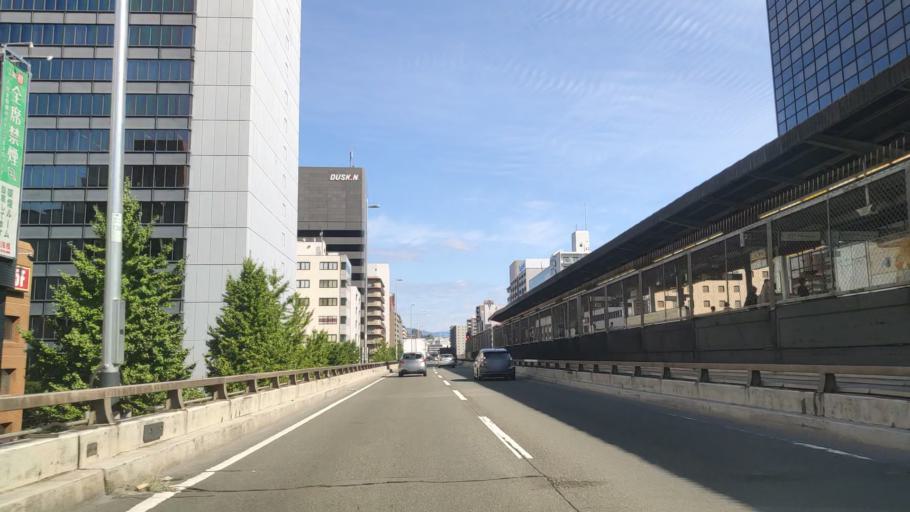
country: JP
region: Osaka
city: Suita
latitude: 34.7587
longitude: 135.4969
